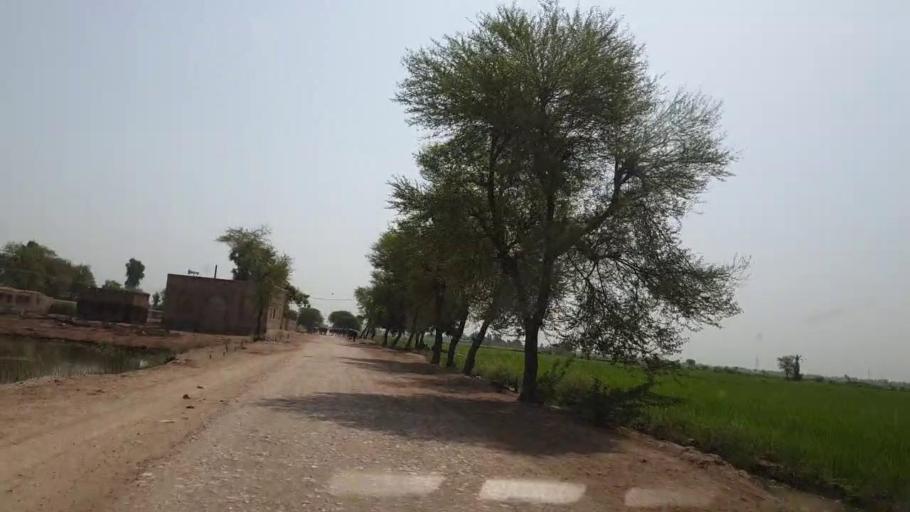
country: PK
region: Sindh
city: Lakhi
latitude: 27.8788
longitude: 68.6632
